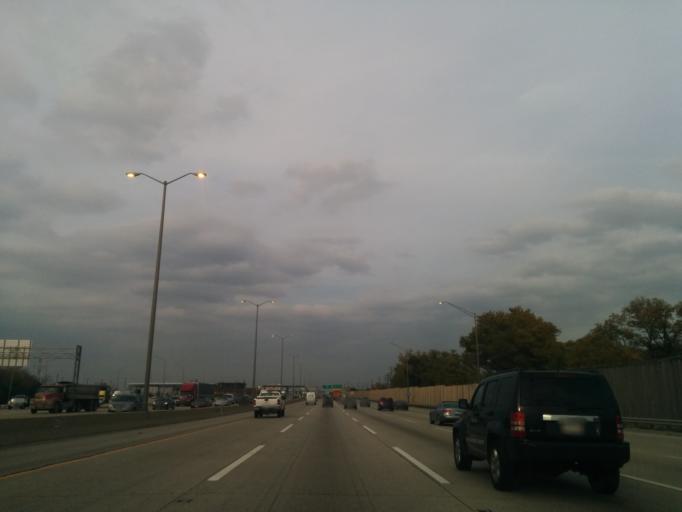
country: US
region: Illinois
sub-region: Cook County
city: Schiller Park
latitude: 41.9597
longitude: -87.8779
